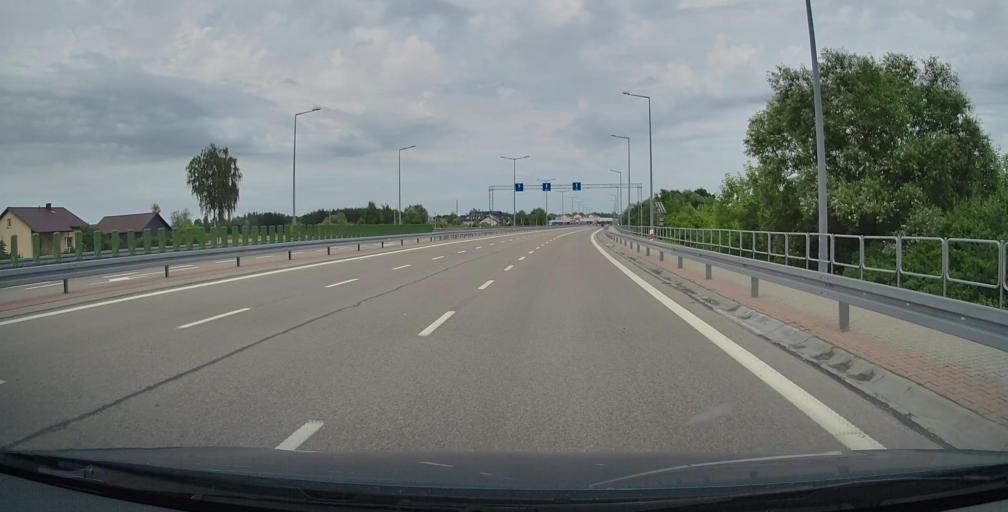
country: PL
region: Lublin Voivodeship
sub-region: Powiat bialski
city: Terespol
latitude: 52.0661
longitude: 23.6345
